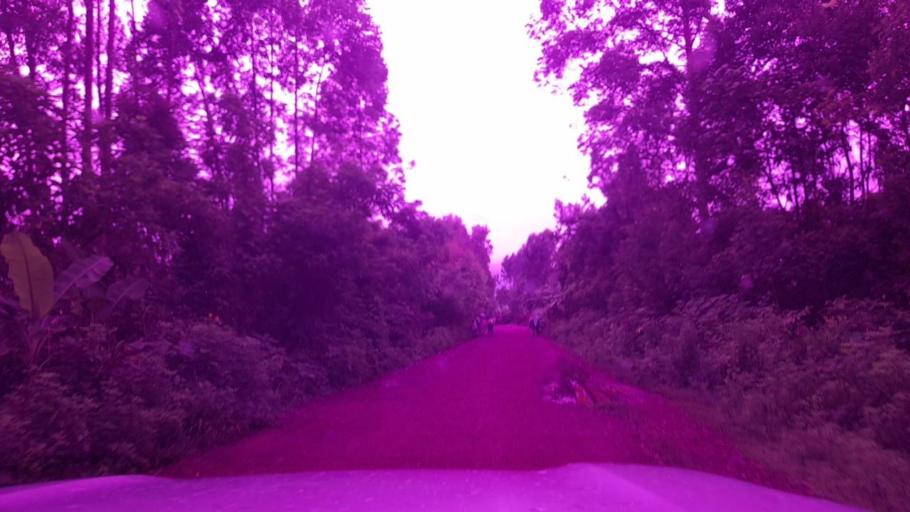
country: ET
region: Southern Nations, Nationalities, and People's Region
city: Bonga
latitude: 7.5881
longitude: 36.0160
